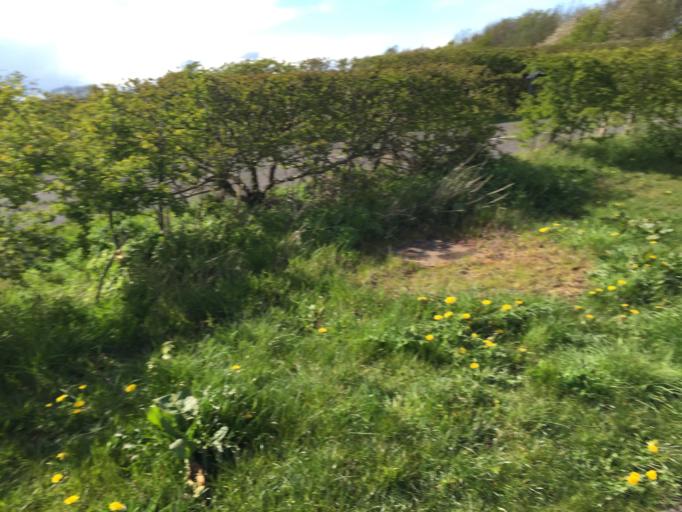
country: GB
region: England
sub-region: Lincolnshire
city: Skellingthorpe
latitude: 53.1224
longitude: -0.6441
